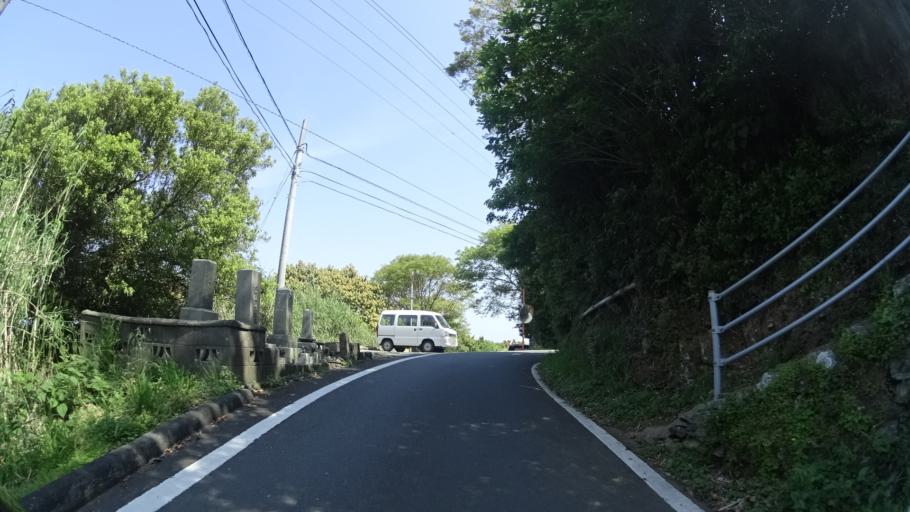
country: JP
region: Ehime
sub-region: Nishiuwa-gun
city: Ikata-cho
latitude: 33.3691
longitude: 132.0494
